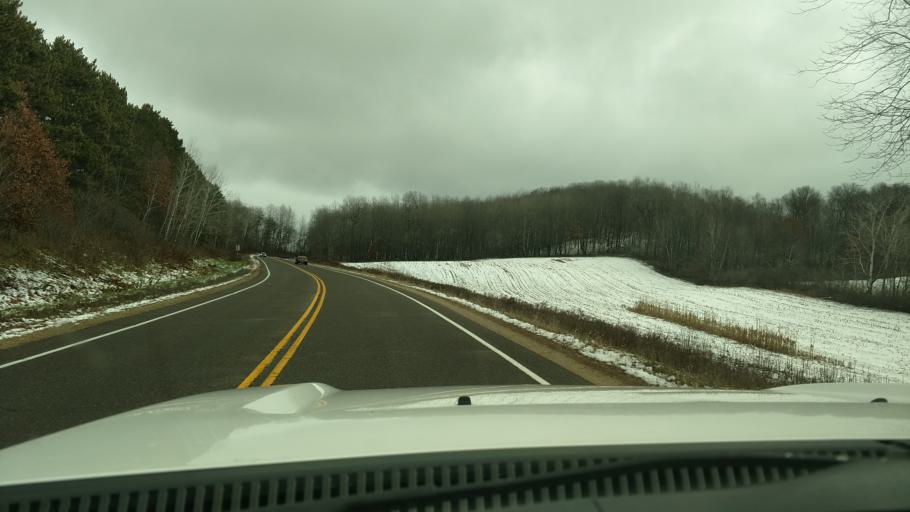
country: US
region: Wisconsin
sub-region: Dunn County
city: Boyceville
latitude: 45.1368
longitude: -91.9506
